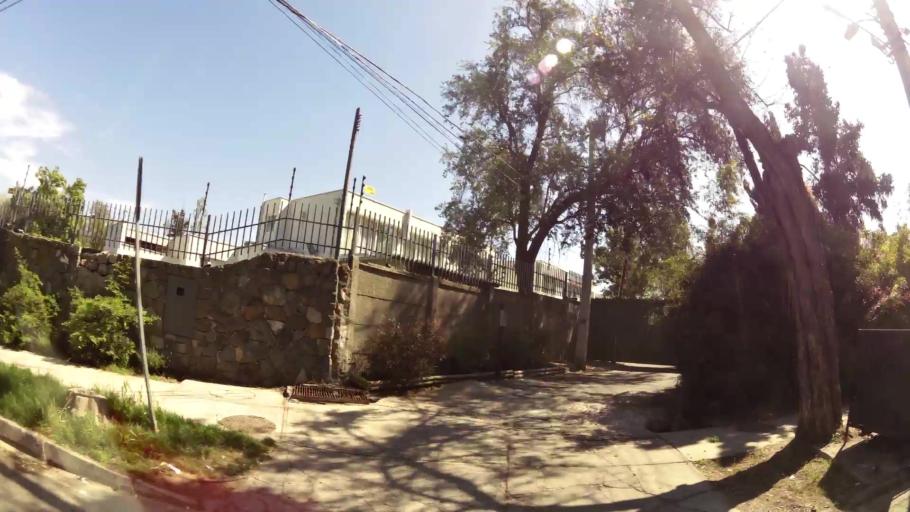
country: CL
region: Santiago Metropolitan
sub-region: Provincia de Santiago
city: Villa Presidente Frei, Nunoa, Santiago, Chile
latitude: -33.4387
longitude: -70.5231
